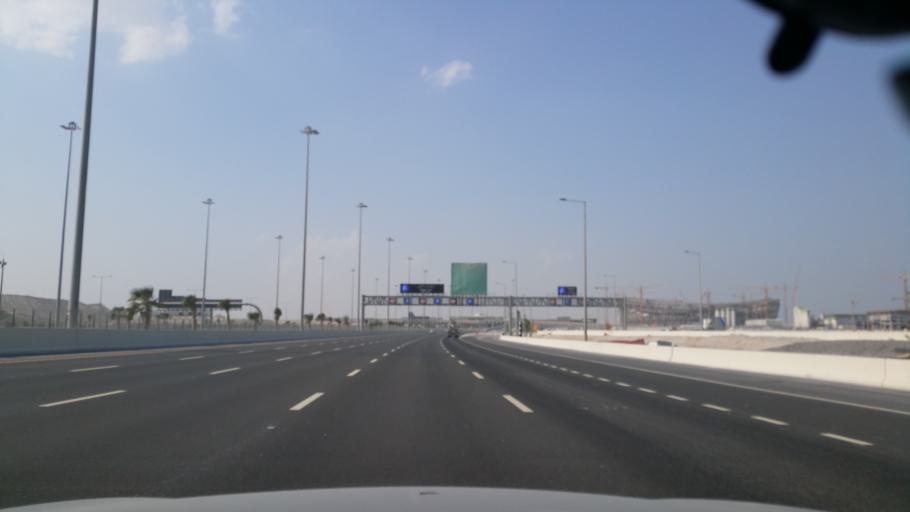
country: QA
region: Baladiyat Umm Salal
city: Umm Salal Muhammad
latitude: 25.4062
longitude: 51.4907
